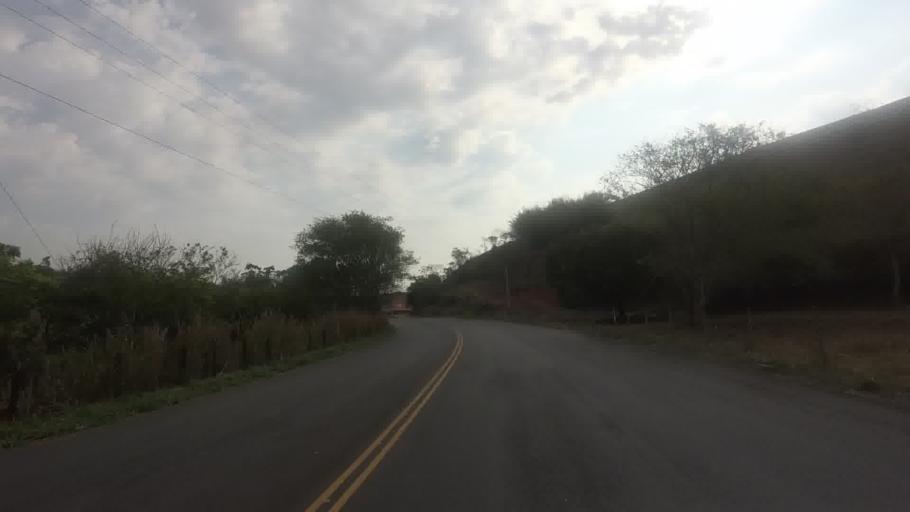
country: BR
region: Rio de Janeiro
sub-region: Itaperuna
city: Itaperuna
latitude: -21.3533
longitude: -41.9164
